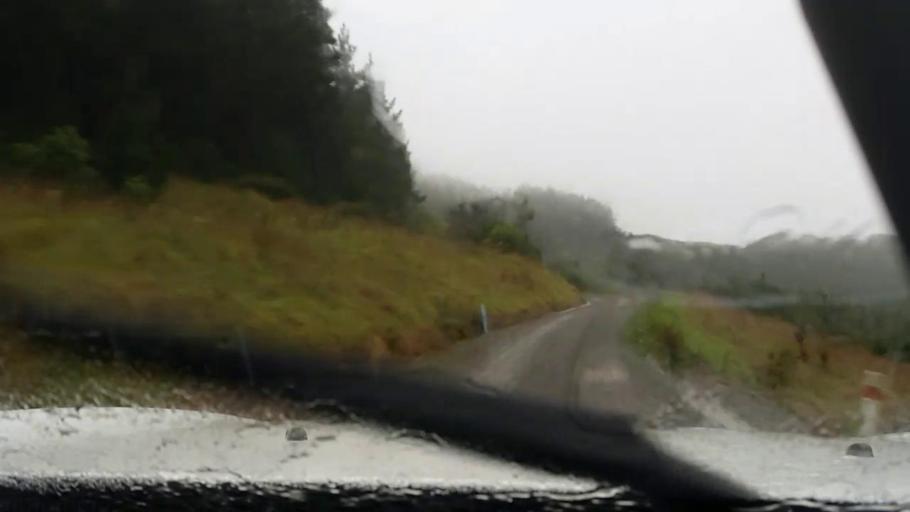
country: NZ
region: Wellington
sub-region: Masterton District
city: Masterton
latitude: -41.1899
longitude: 175.8170
